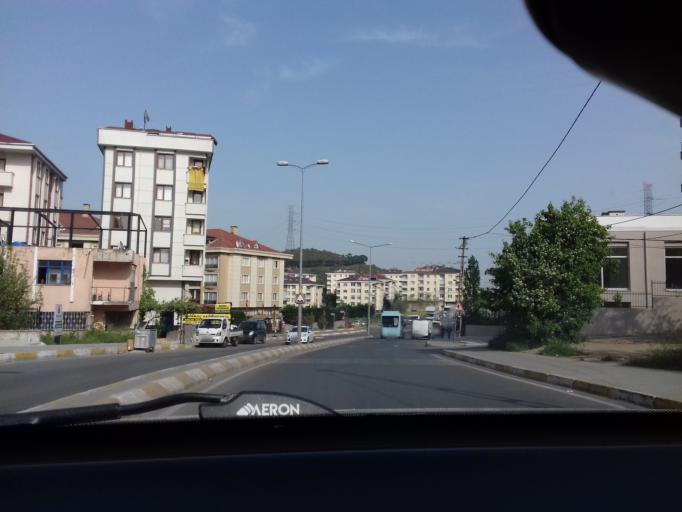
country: TR
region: Istanbul
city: Pendik
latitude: 40.9078
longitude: 29.2588
